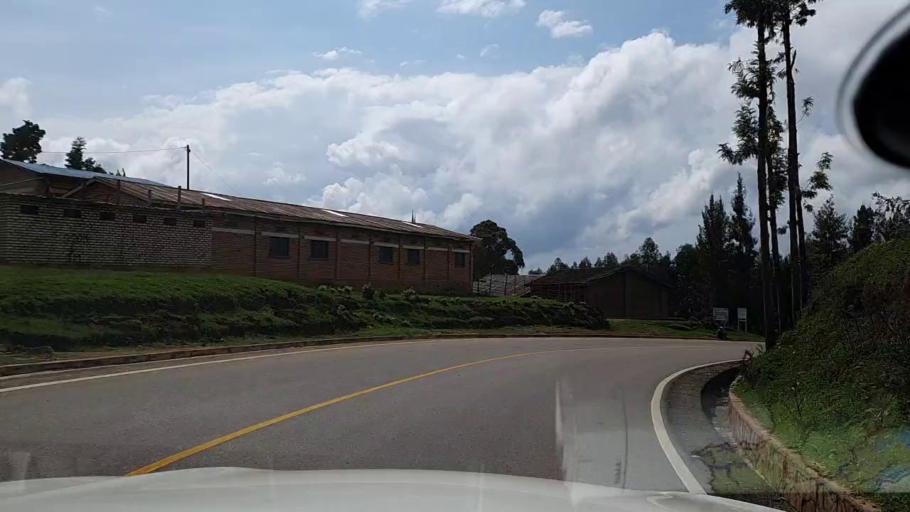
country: RW
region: Southern Province
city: Nzega
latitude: -2.5018
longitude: 29.5106
